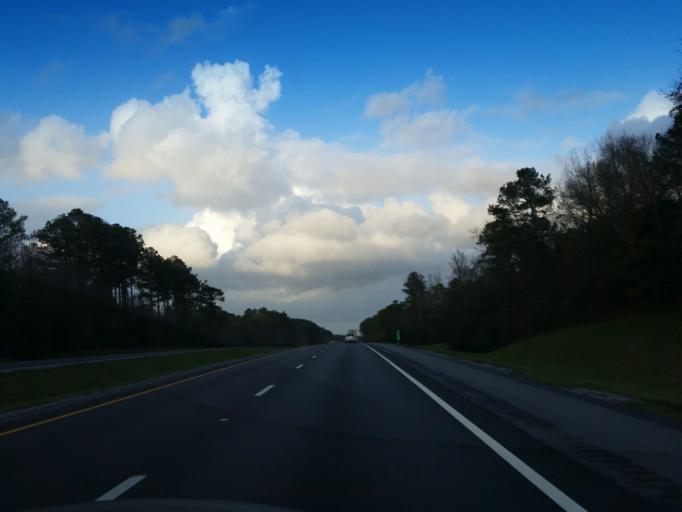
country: US
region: Mississippi
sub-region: Jones County
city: Sharon
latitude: 31.8867
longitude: -89.0366
